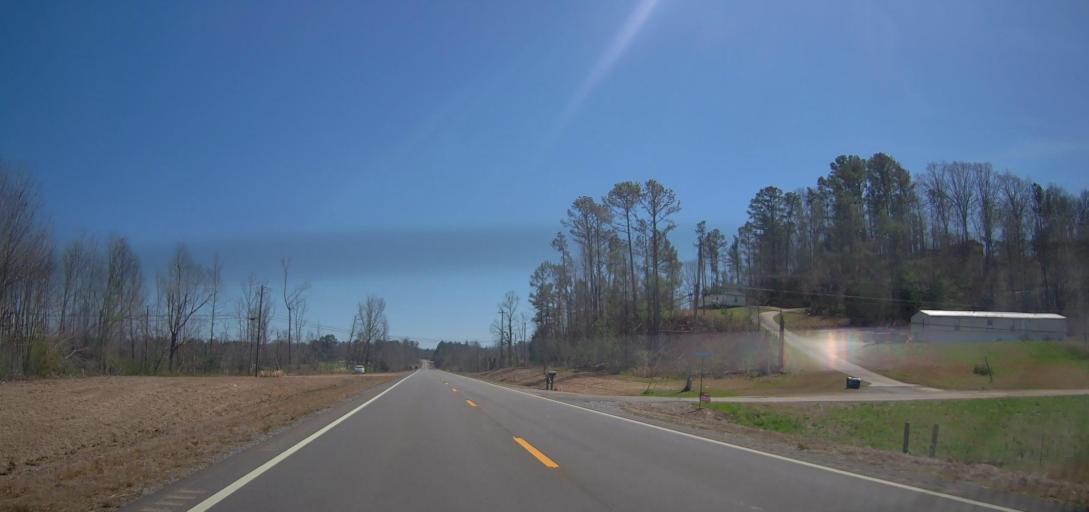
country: US
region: Alabama
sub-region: Calhoun County
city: Ohatchee
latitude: 33.7775
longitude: -85.9972
